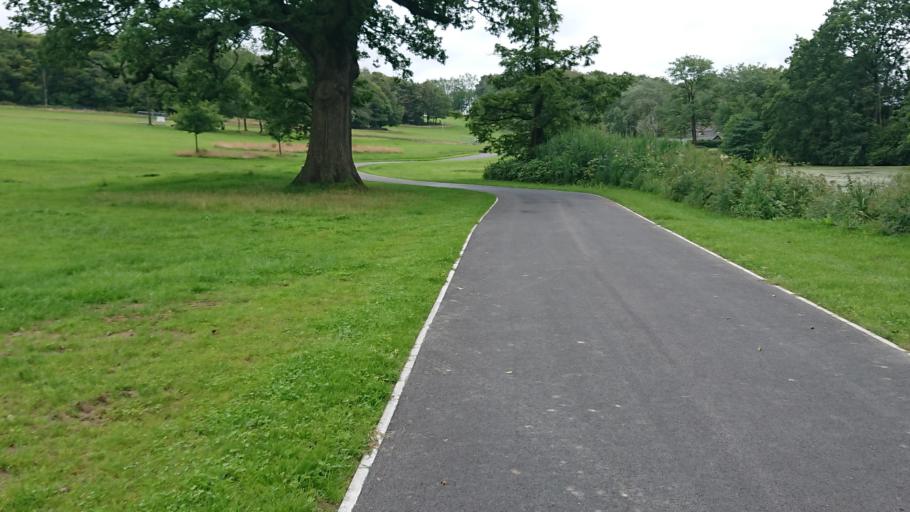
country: GB
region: England
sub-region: Lancashire
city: Galgate
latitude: 54.0141
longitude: -2.7907
